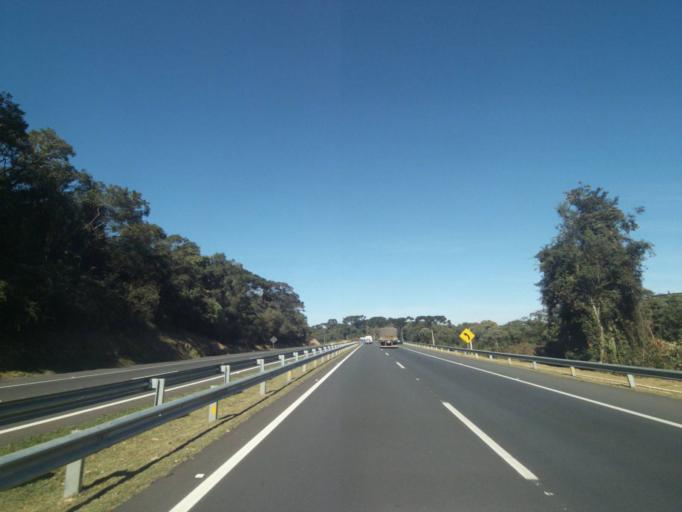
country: BR
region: Parana
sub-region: Carambei
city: Carambei
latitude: -24.9041
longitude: -50.4225
